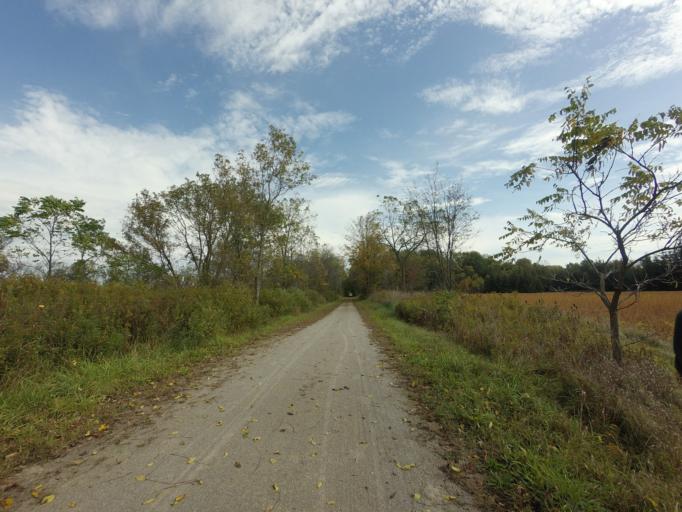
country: CA
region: Ontario
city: Brantford
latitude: 43.1880
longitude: -80.1406
